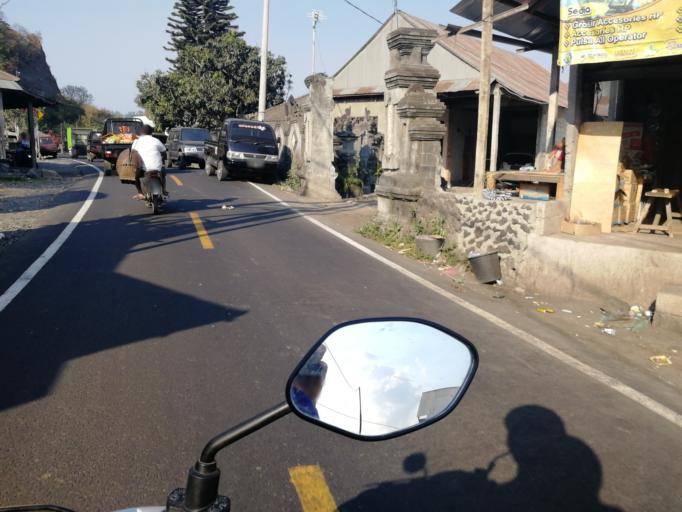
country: ID
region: Bali
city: Banjar Trunyan
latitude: -8.2411
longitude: 115.4046
